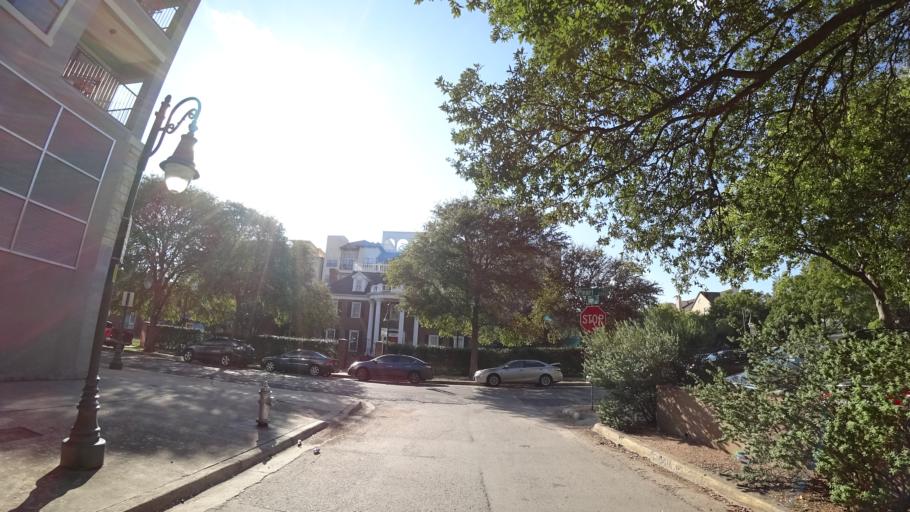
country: US
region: Texas
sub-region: Travis County
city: Austin
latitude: 30.2901
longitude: -97.7465
